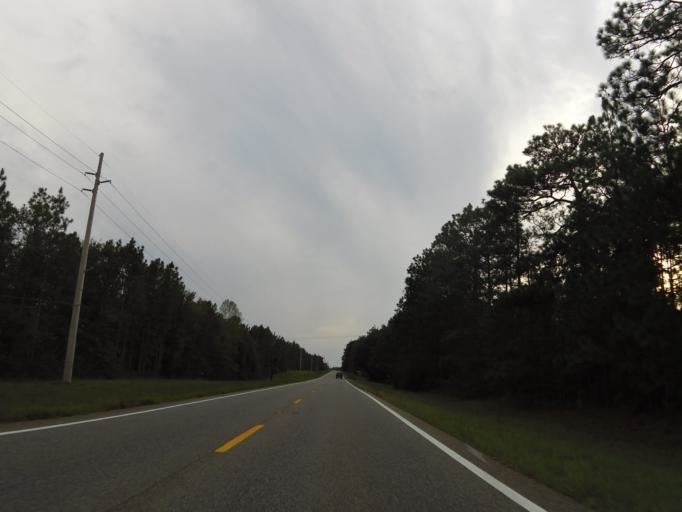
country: US
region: Alabama
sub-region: Baldwin County
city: Bay Minette
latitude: 30.9044
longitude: -87.7298
